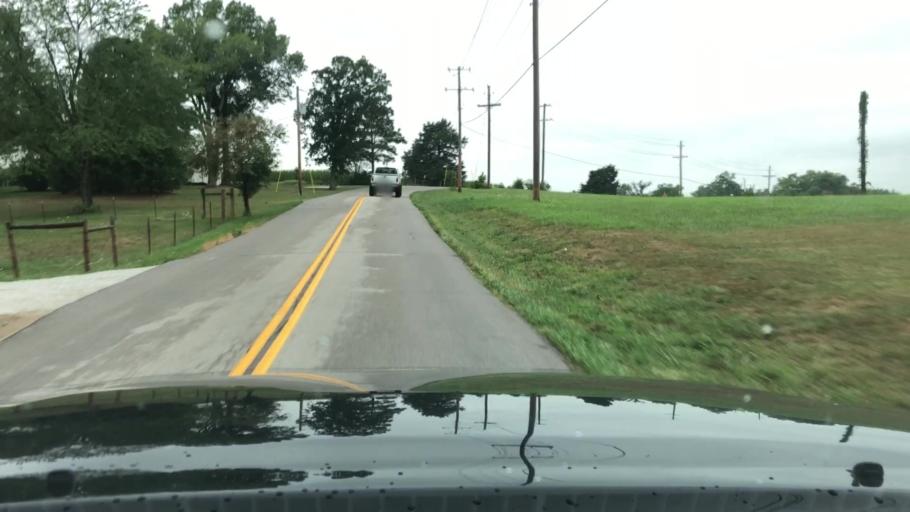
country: US
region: Missouri
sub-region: Saint Charles County
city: Wentzville
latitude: 38.8475
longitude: -90.8839
